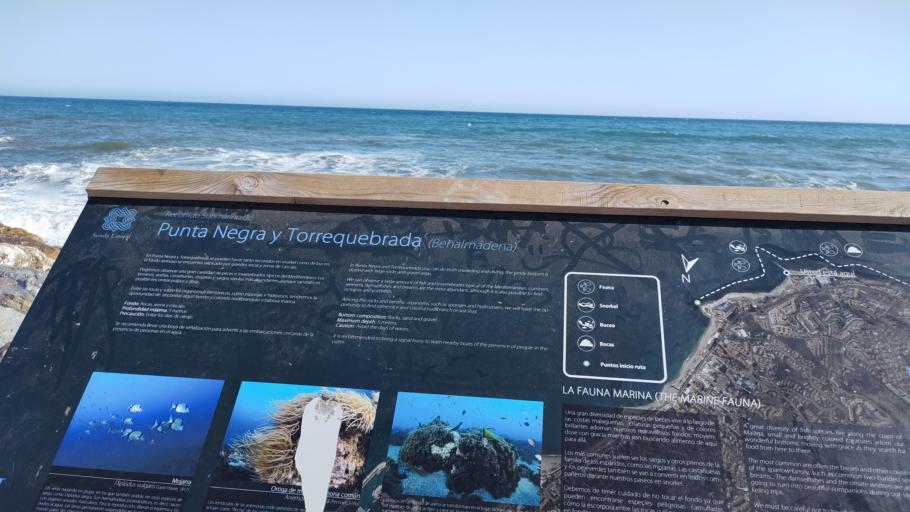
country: ES
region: Andalusia
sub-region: Provincia de Malaga
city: Benalmadena
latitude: 36.5794
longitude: -4.5399
